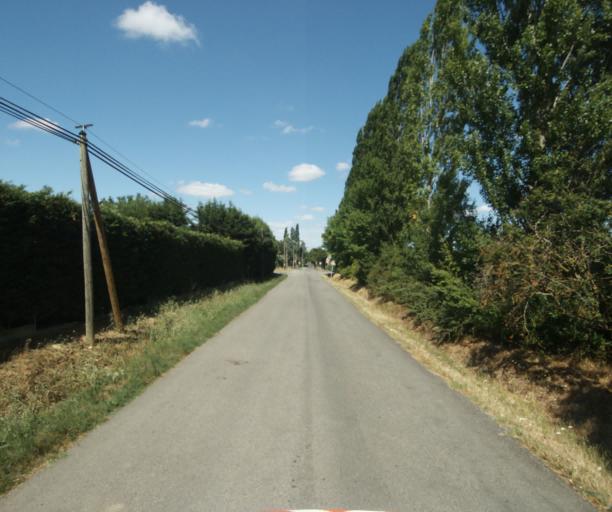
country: FR
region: Midi-Pyrenees
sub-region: Departement de la Haute-Garonne
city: Revel
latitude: 43.4877
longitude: 2.0162
